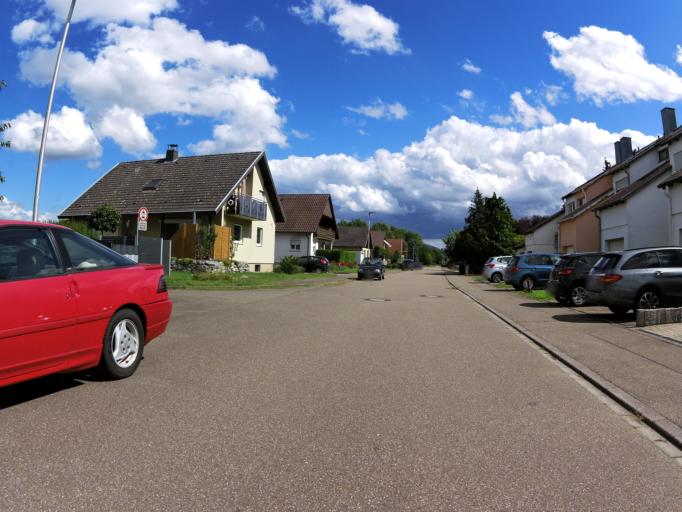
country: DE
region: Baden-Wuerttemberg
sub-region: Freiburg Region
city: Lahr
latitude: 48.3655
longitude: 7.8362
